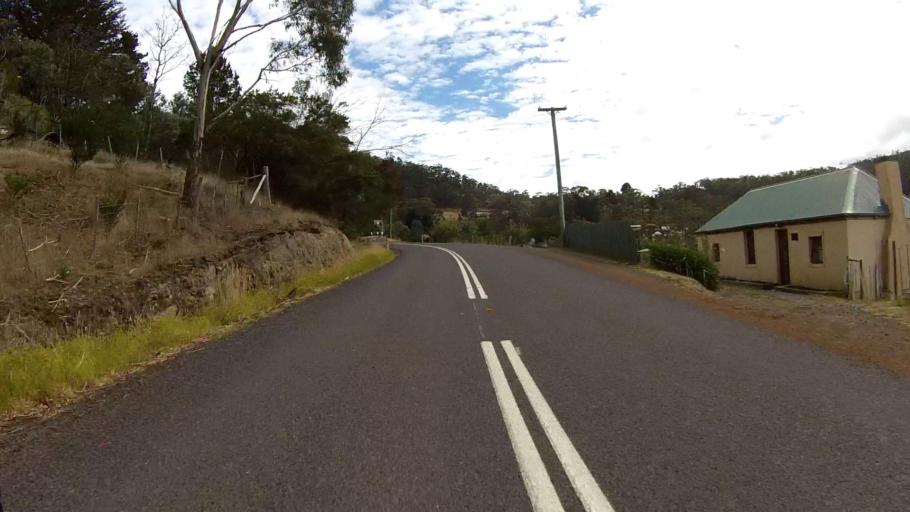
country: AU
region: Tasmania
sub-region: Clarence
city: Lindisfarne
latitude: -42.7869
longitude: 147.3597
